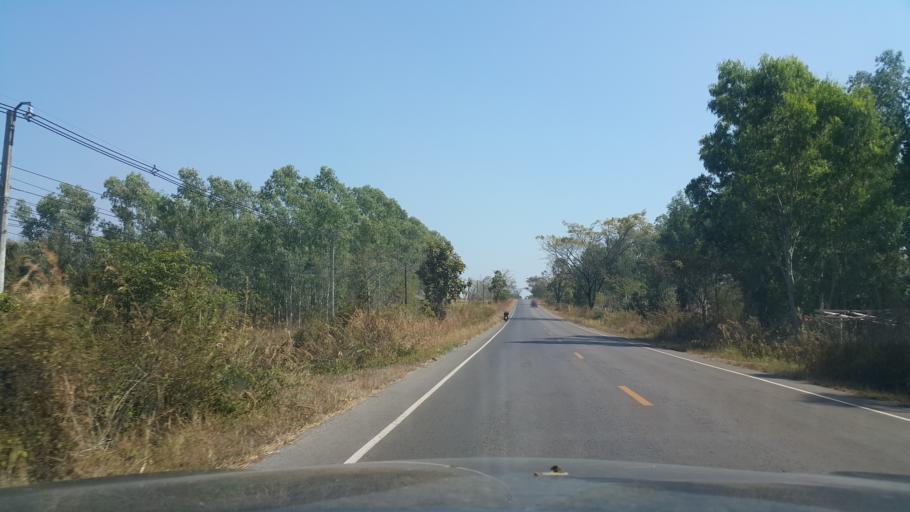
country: TH
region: Changwat Udon Thani
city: Ban Dung
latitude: 17.6086
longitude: 103.2679
